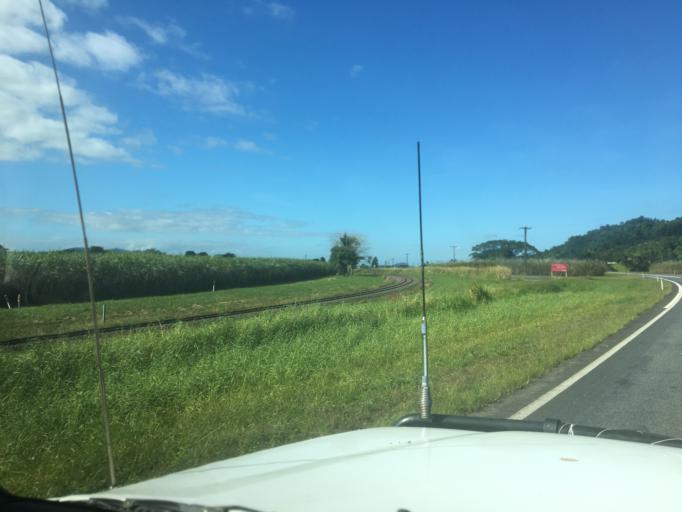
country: AU
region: Queensland
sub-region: Cassowary Coast
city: Innisfail
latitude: -17.3098
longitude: 145.9256
